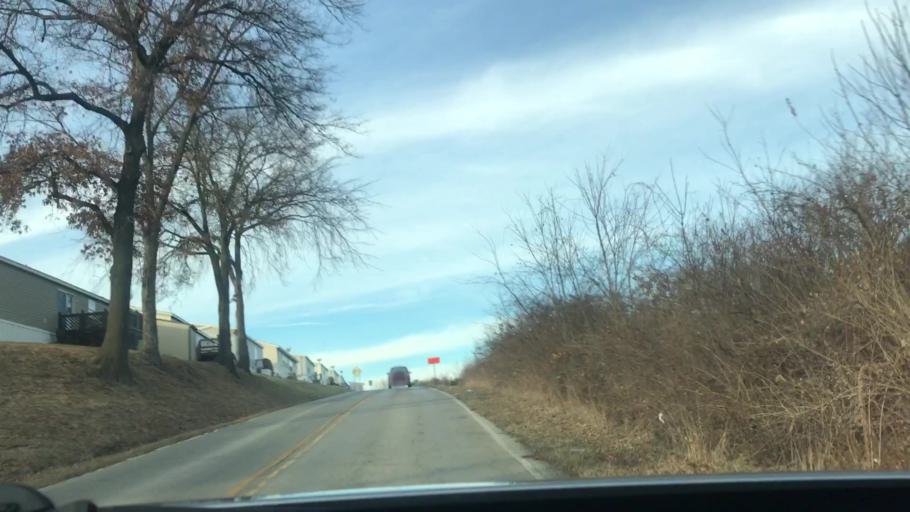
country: US
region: Missouri
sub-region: Platte County
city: Riverside
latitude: 39.2001
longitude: -94.5902
